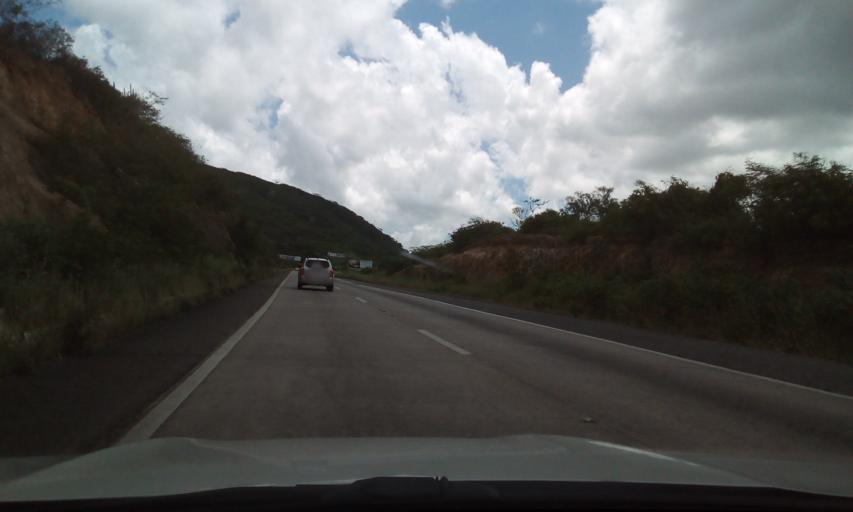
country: BR
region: Pernambuco
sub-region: Pombos
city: Pombos
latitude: -8.1582
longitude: -35.4310
